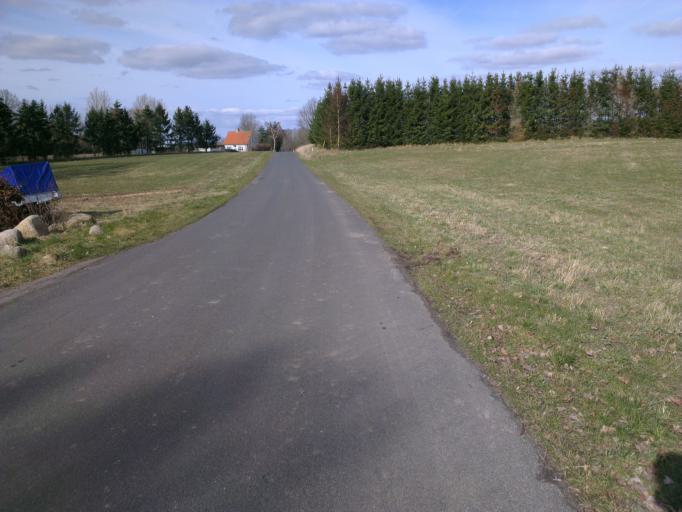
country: DK
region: Zealand
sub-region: Roskilde Kommune
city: Jyllinge
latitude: 55.7627
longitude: 12.0528
